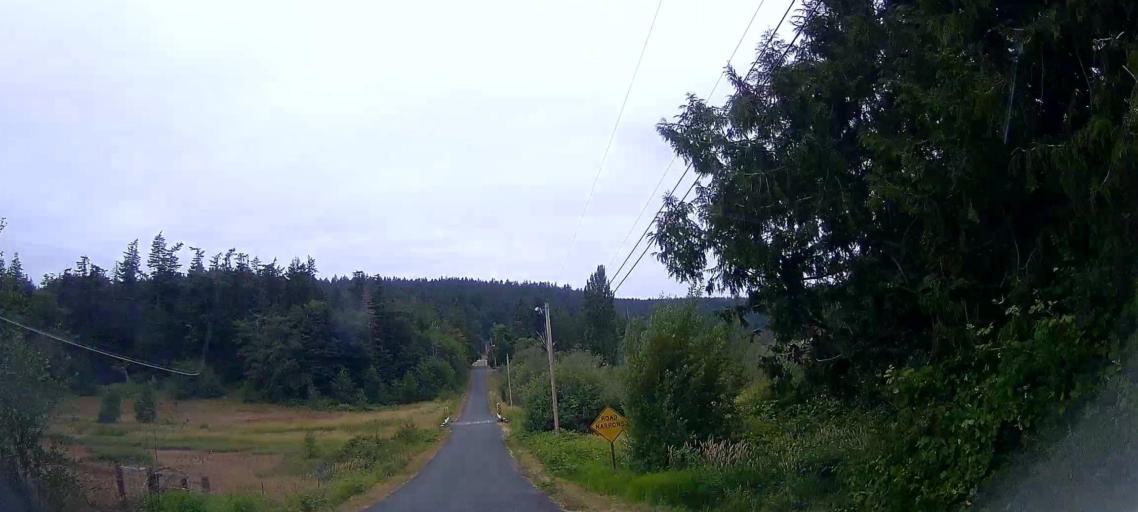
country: US
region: Washington
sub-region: Skagit County
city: Anacortes
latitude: 48.4336
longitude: -122.6149
